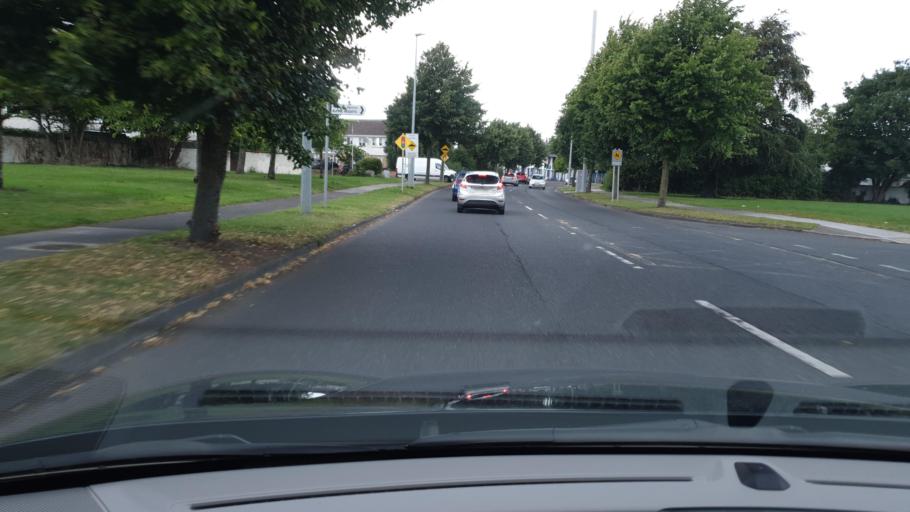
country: IE
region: Leinster
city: Clondalkin
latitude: 53.3234
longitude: -6.4107
